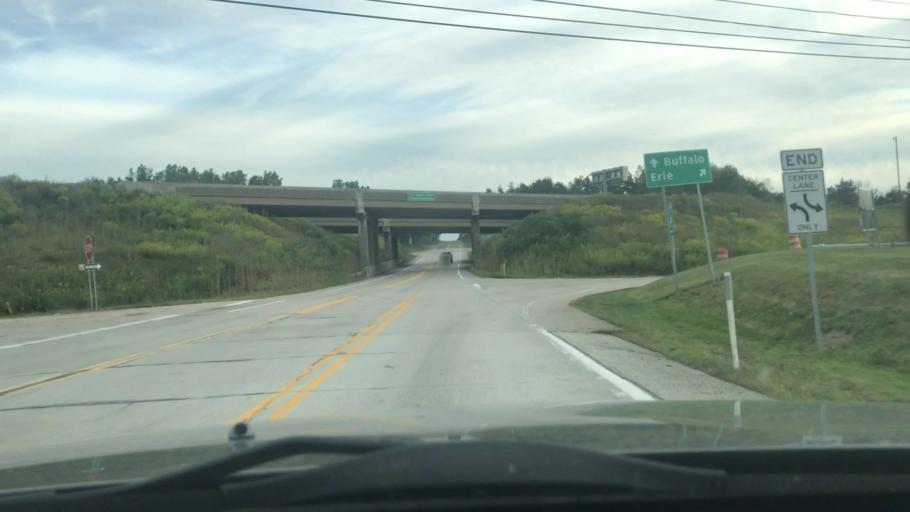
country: US
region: Pennsylvania
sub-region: Erie County
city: Northwest Harborcreek
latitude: 42.1406
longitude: -79.9235
